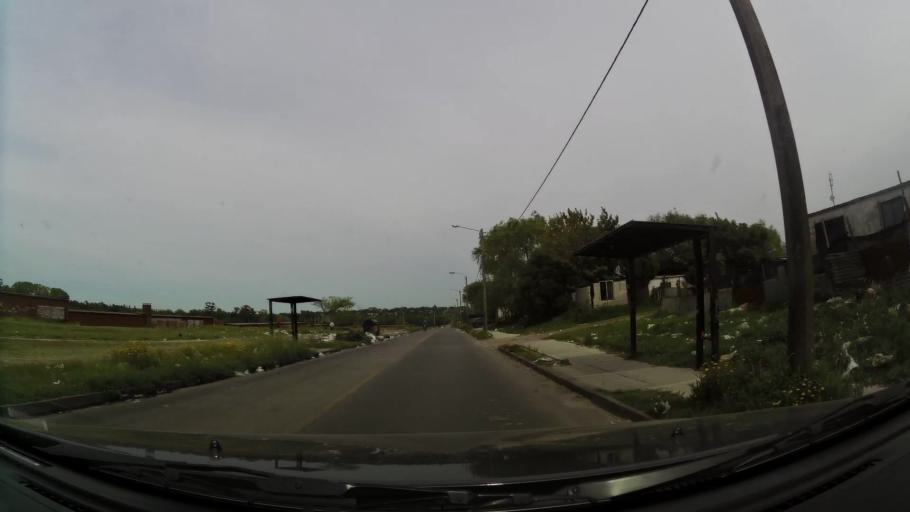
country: UY
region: Montevideo
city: Montevideo
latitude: -34.8363
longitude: -56.1760
